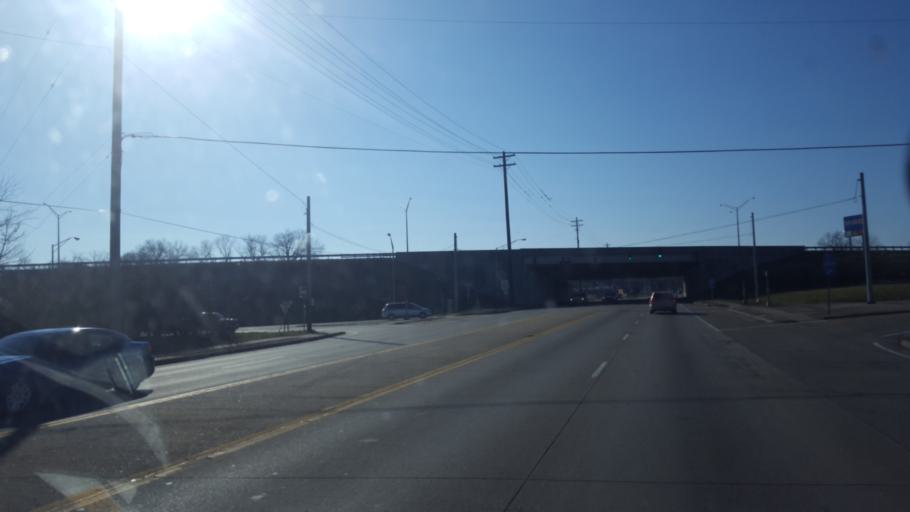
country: US
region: Kentucky
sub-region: Jefferson County
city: Shively
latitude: 38.1901
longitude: -85.7835
